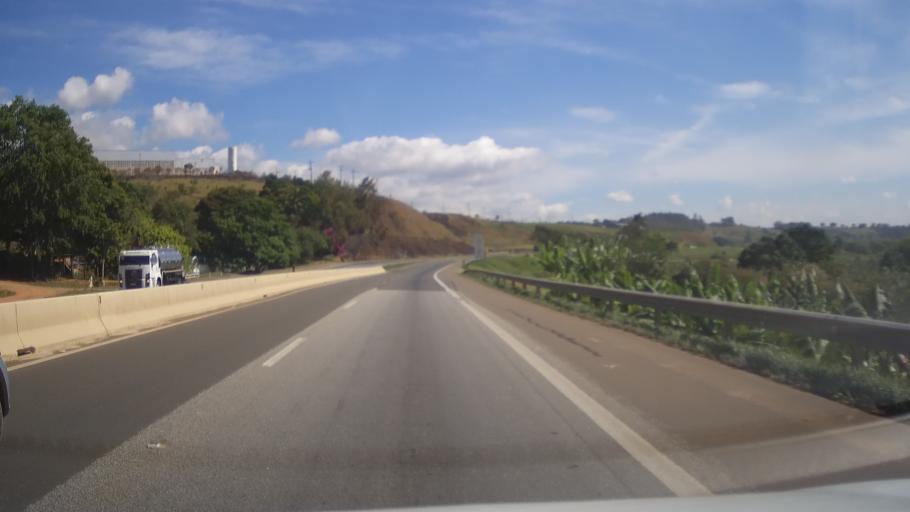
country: BR
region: Minas Gerais
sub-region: Cambui
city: Cambui
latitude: -22.5500
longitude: -46.0396
